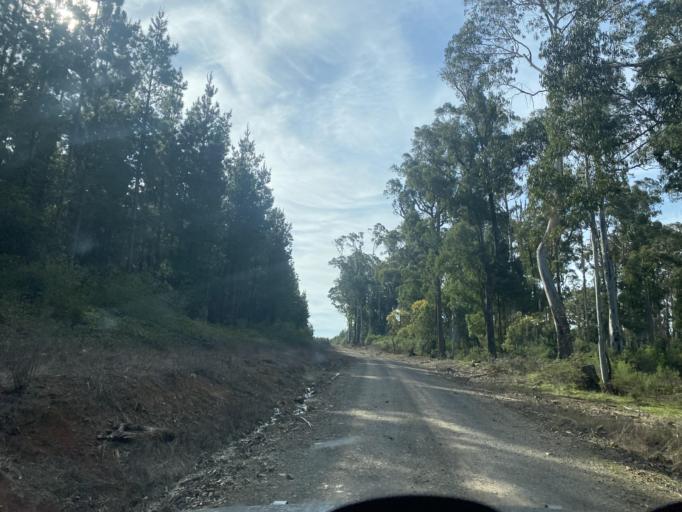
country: AU
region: Victoria
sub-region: Mansfield
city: Mansfield
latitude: -36.8796
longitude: 146.1884
